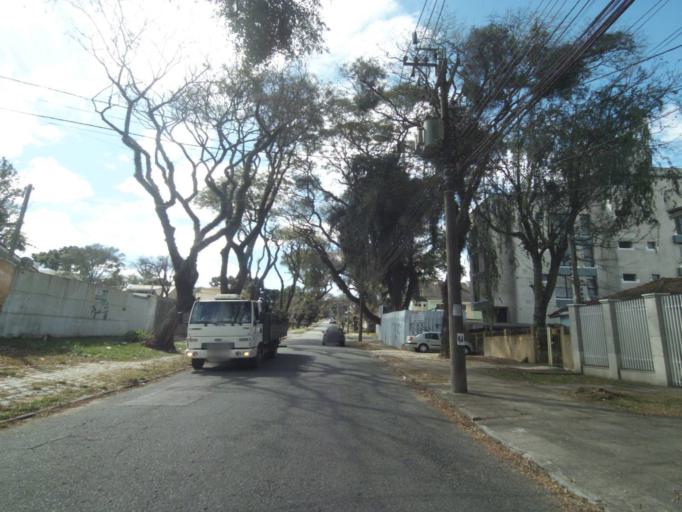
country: BR
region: Parana
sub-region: Curitiba
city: Curitiba
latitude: -25.4595
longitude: -49.2763
